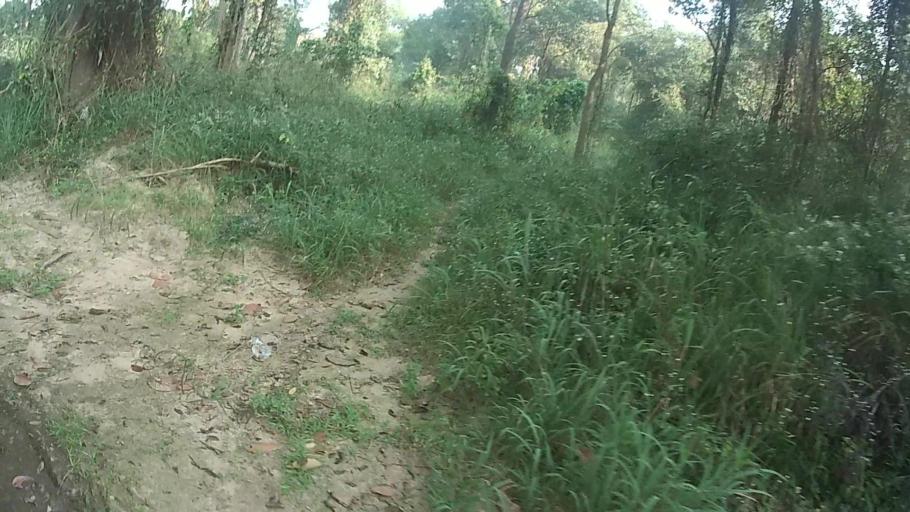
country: TH
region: Chiang Mai
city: San Sai
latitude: 18.9319
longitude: 99.0445
